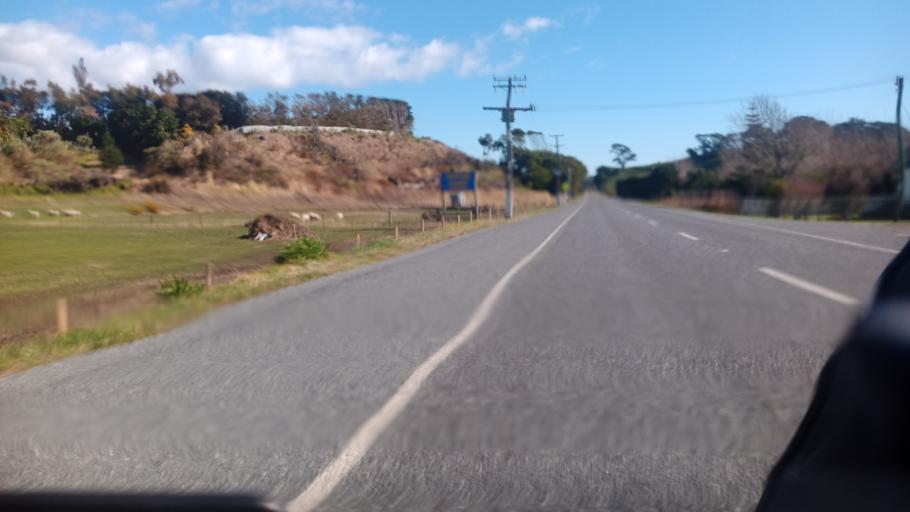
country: NZ
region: Bay of Plenty
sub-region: Opotiki District
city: Opotiki
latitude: -37.9889
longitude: 177.3526
